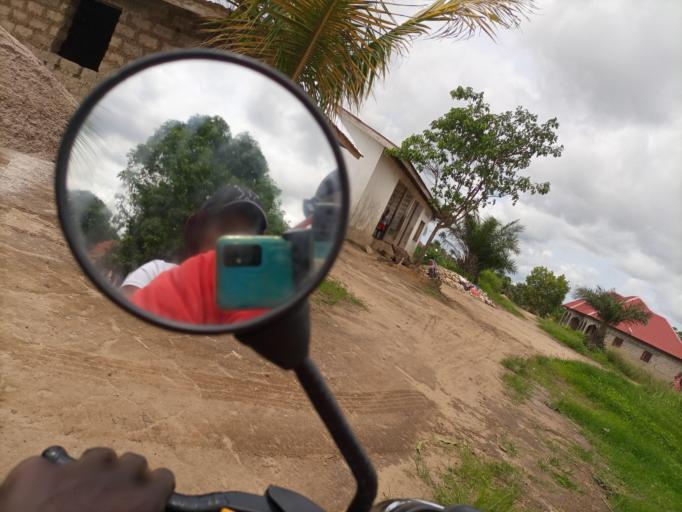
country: SL
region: Southern Province
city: Baoma
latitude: 7.9683
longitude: -11.7112
